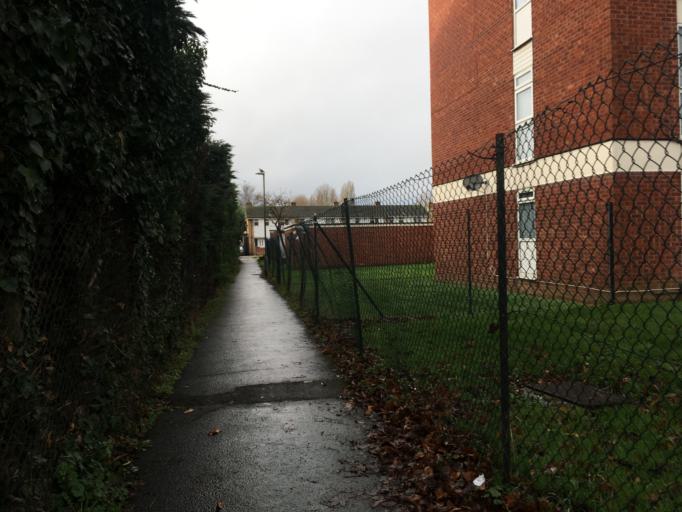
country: GB
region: England
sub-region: West Berkshire
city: Tilehurst
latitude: 51.4429
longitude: -1.0193
